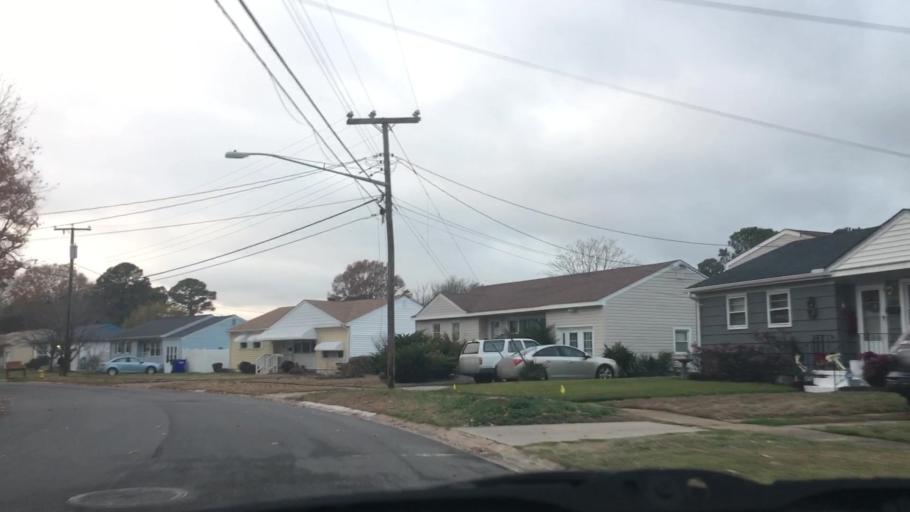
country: US
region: Virginia
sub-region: City of Norfolk
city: Norfolk
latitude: 36.9290
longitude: -76.2326
